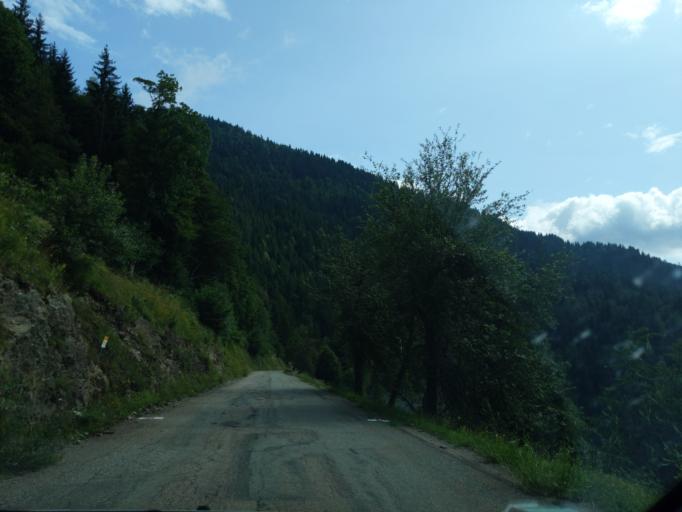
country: FR
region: Rhone-Alpes
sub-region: Departement de la Savoie
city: Ugine
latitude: 45.7492
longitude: 6.4711
